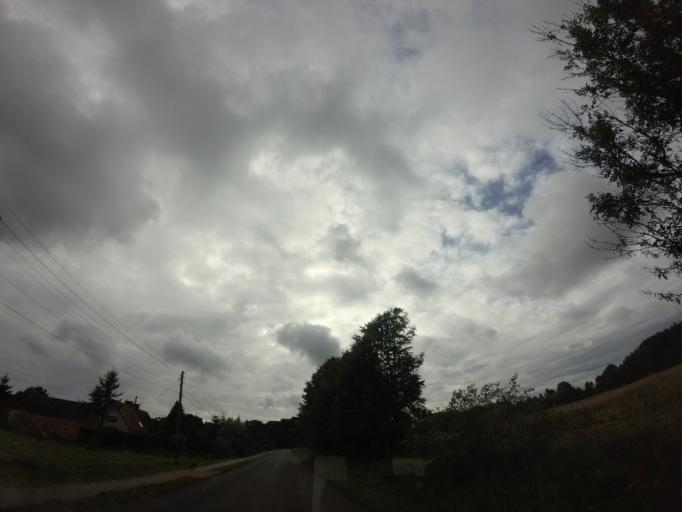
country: PL
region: West Pomeranian Voivodeship
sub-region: Powiat goleniowski
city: Stepnica
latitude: 53.6550
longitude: 14.6544
